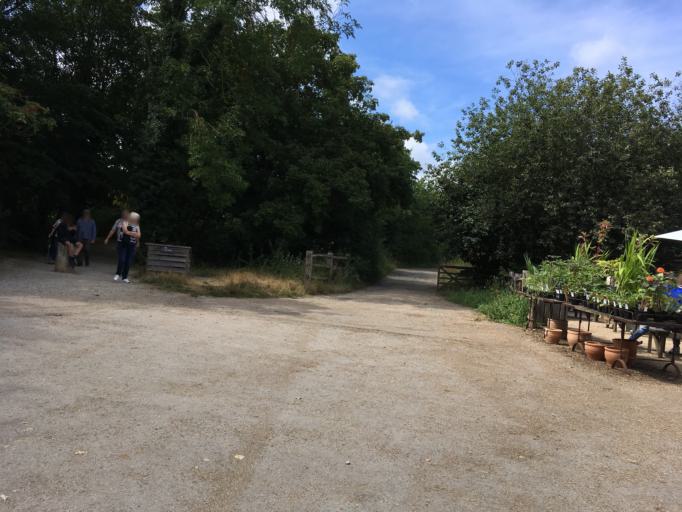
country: GB
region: England
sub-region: Kent
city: Cranbrook
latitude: 51.1165
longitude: 0.5796
